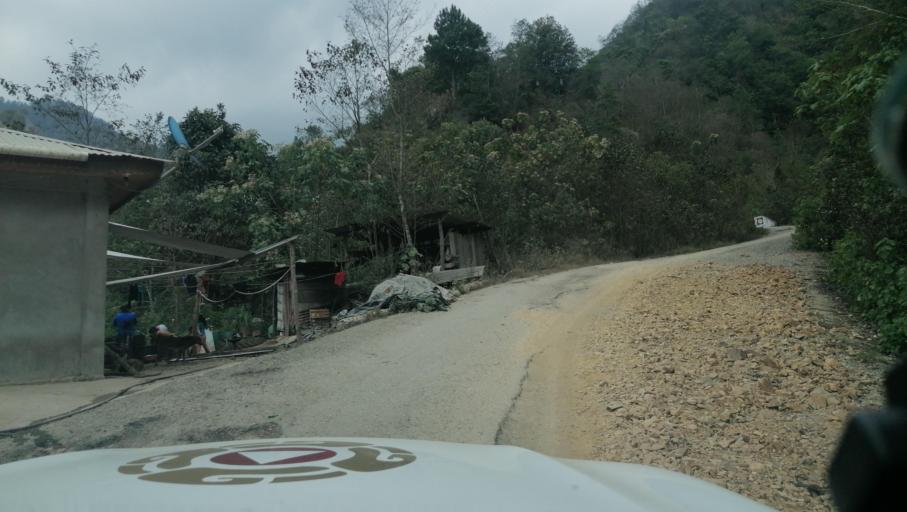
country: GT
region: San Marcos
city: Tacana
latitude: 15.2221
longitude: -92.1971
